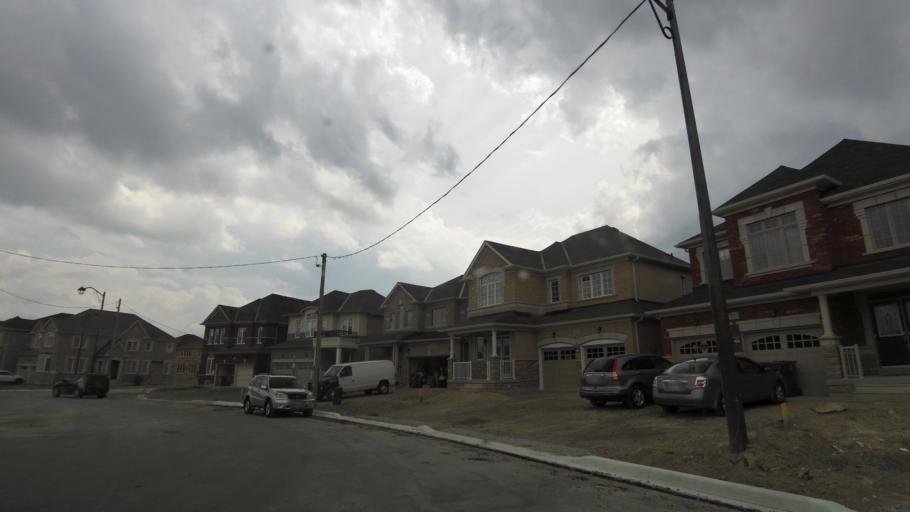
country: CA
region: Ontario
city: Brampton
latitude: 43.7535
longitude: -79.8404
